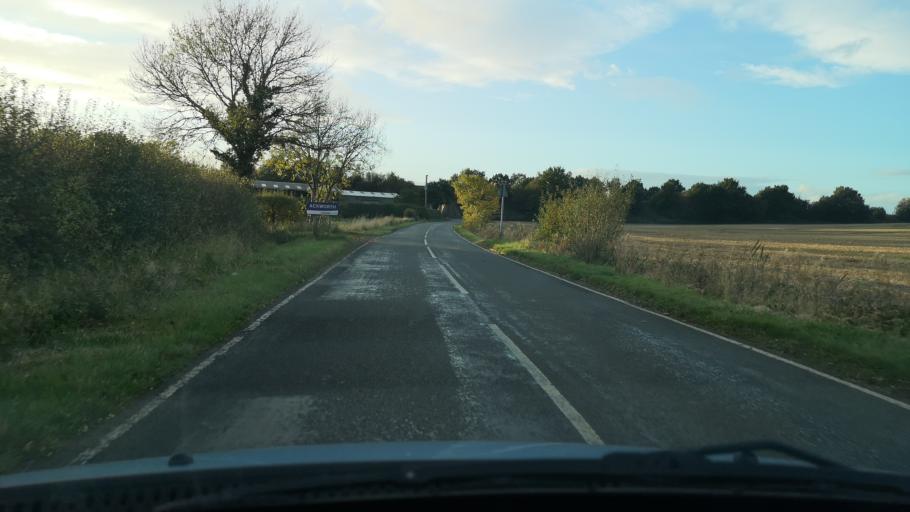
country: GB
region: England
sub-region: City and Borough of Wakefield
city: Low Ackworth
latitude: 53.6498
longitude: -1.3109
